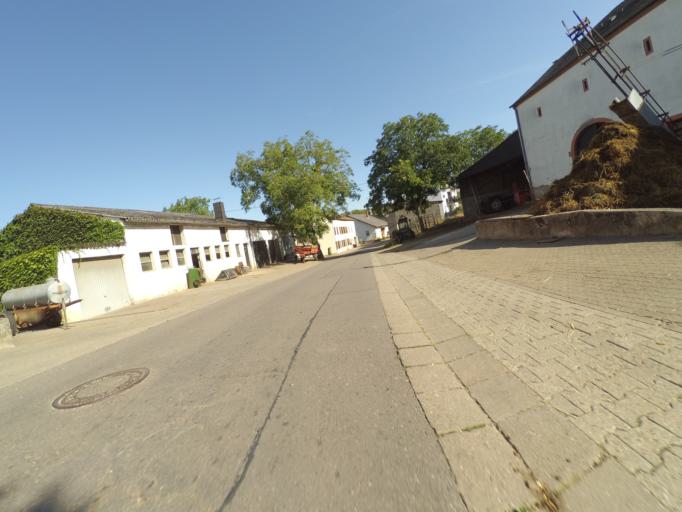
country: DE
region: Saarland
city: Perl
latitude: 49.5043
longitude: 6.4061
